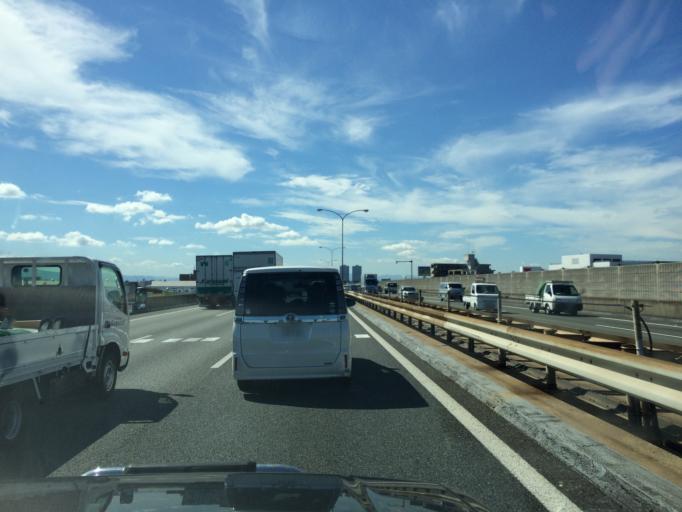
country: JP
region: Osaka
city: Yao
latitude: 34.6529
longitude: 135.5979
